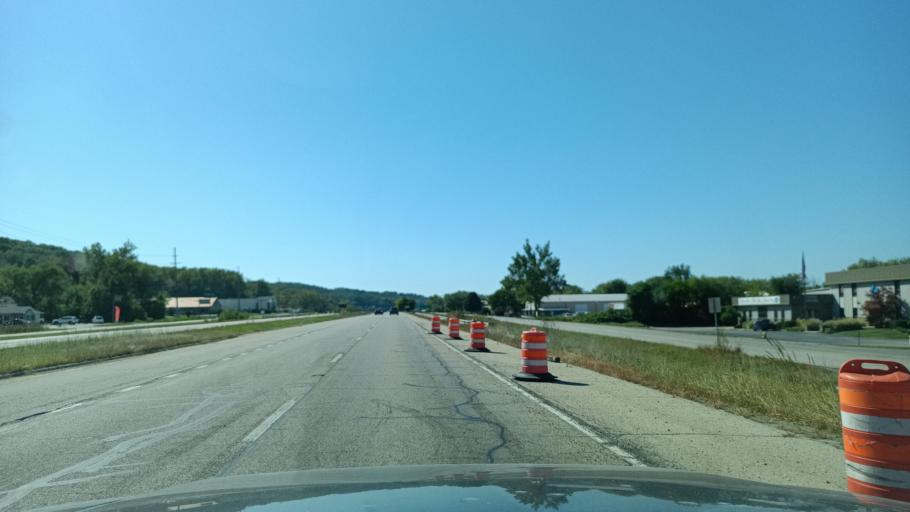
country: US
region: Illinois
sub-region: Peoria County
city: North Peoria
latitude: 40.7052
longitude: -89.5355
